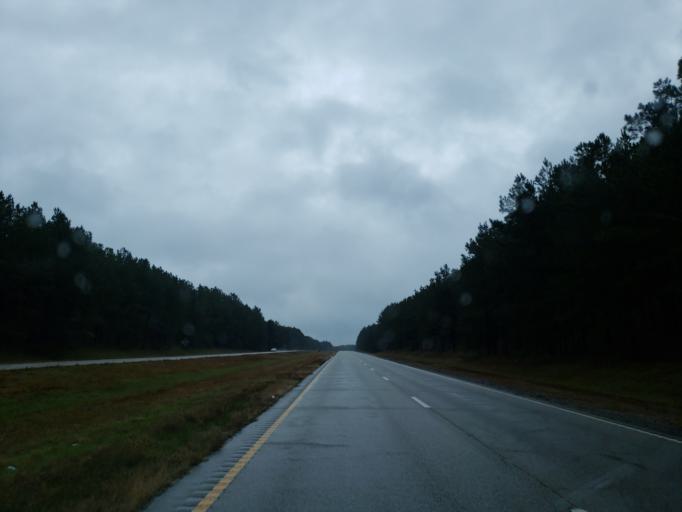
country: US
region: Mississippi
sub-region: Lauderdale County
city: Meridian
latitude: 32.2909
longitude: -88.6970
